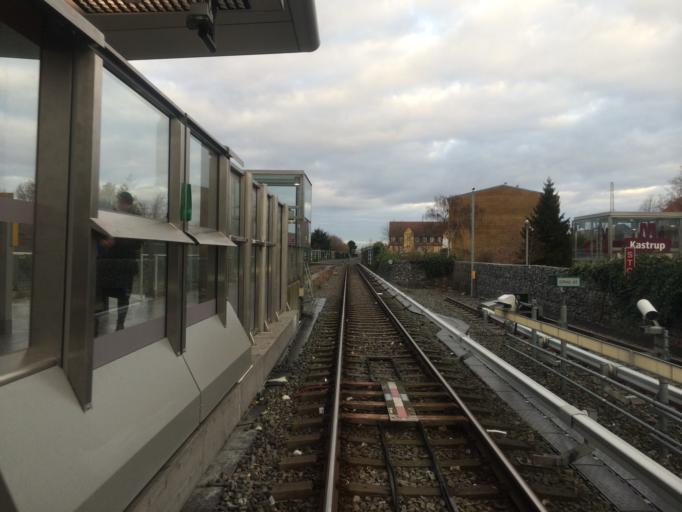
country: DK
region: Capital Region
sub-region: Dragor Kommune
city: Dragor
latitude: 55.6356
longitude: 12.6470
